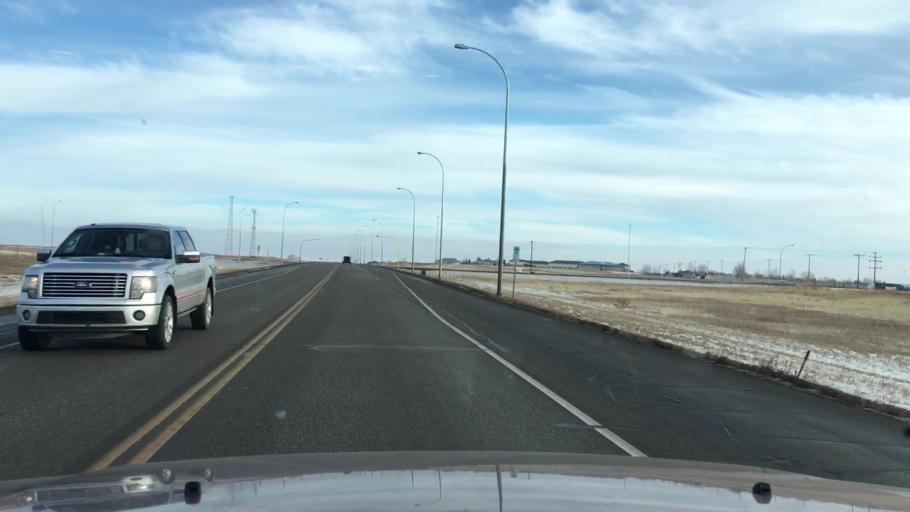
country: CA
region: Saskatchewan
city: Pilot Butte
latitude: 50.4849
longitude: -104.4377
